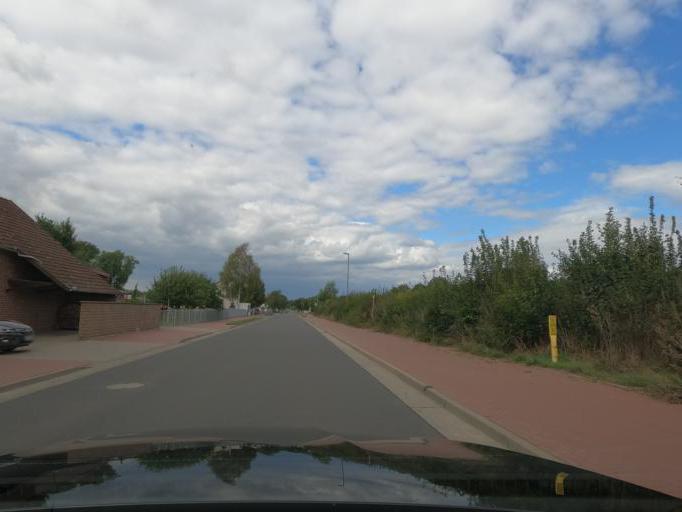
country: DE
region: Lower Saxony
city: Algermissen
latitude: 52.2566
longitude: 9.9638
